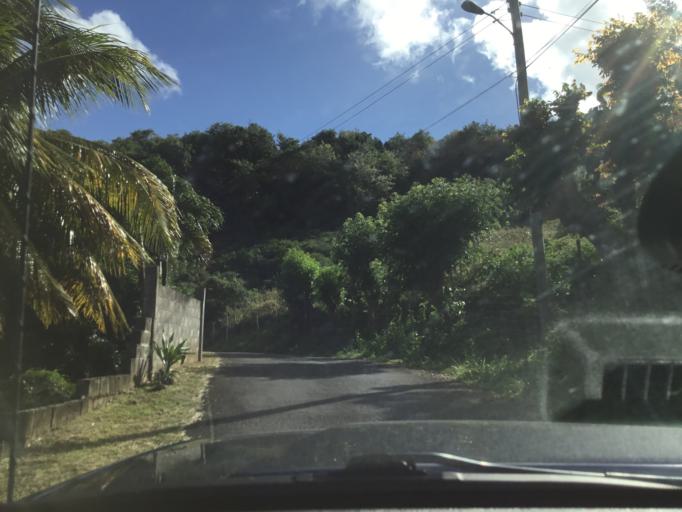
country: VC
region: Saint George
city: Kingstown
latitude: 13.1476
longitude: -61.1762
